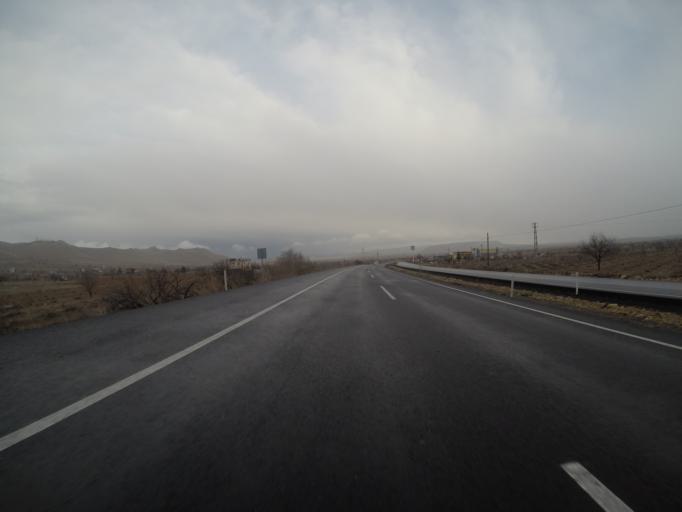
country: TR
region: Nevsehir
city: Goereme
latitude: 38.6781
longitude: 34.7790
